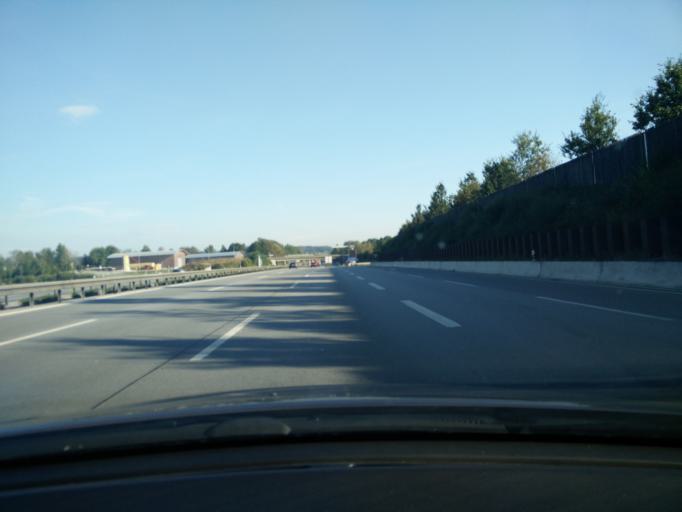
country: DE
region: Bavaria
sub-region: Upper Bavaria
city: Allershausen
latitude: 48.4255
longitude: 11.5896
